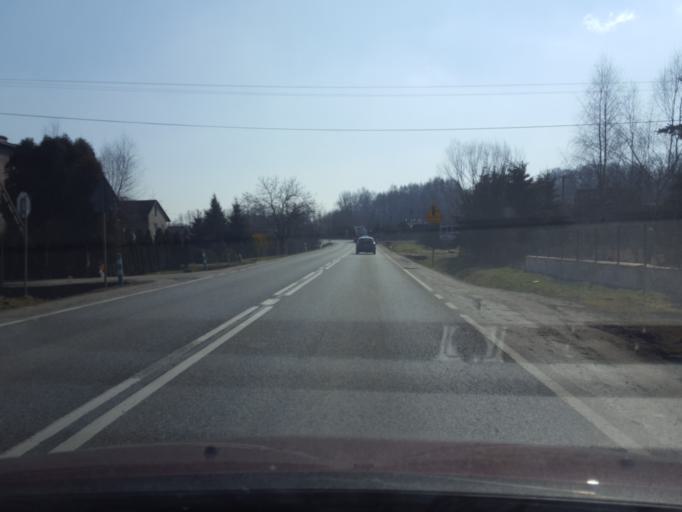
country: PL
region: Lesser Poland Voivodeship
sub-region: Powiat brzeski
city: Czchow
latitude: 49.8514
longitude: 20.6756
